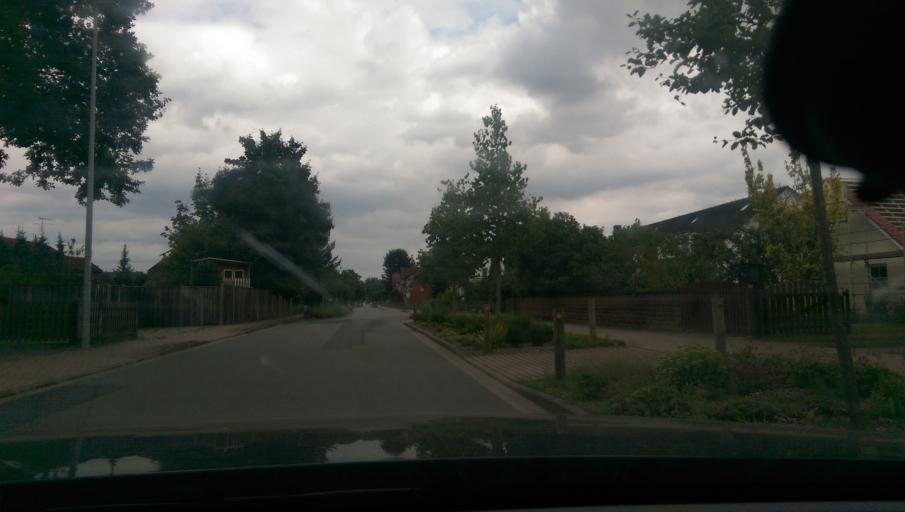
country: DE
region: Lower Saxony
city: Winsen (Aller)
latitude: 52.6708
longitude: 9.8914
